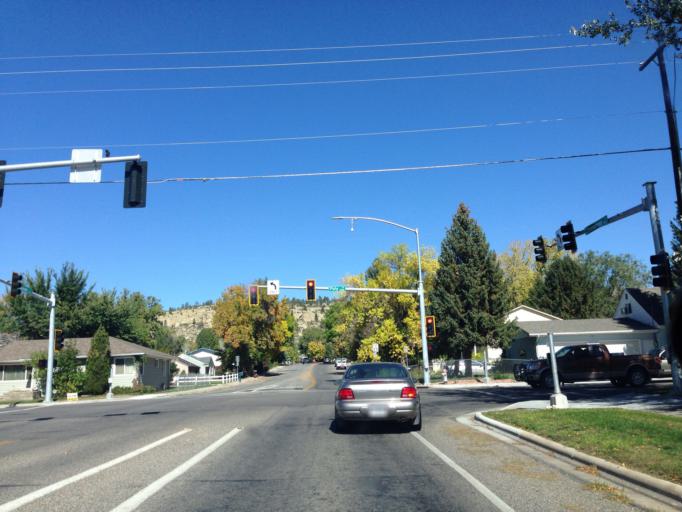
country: US
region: Montana
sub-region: Yellowstone County
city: Billings
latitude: 45.7947
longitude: -108.6015
